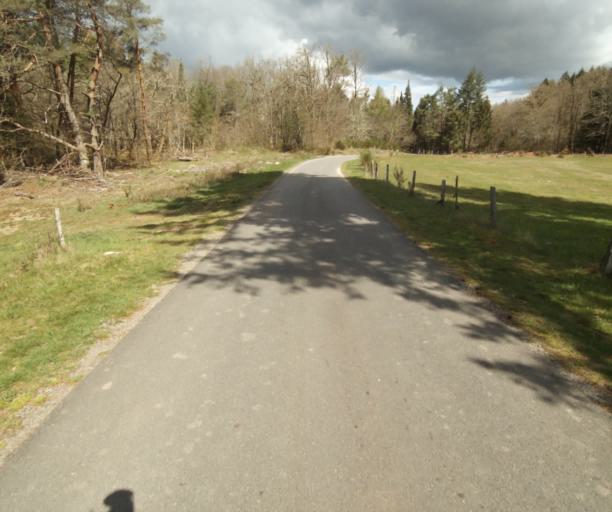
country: FR
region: Limousin
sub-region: Departement de la Correze
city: Correze
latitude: 45.2757
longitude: 1.8973
